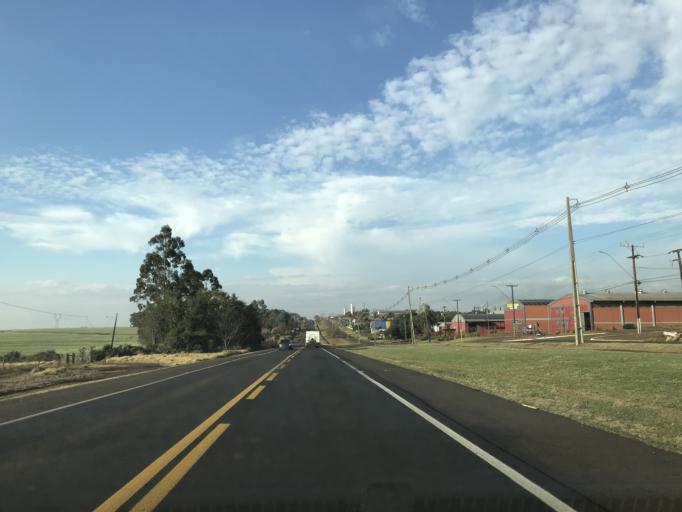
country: BR
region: Parana
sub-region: Cascavel
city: Cascavel
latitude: -25.0428
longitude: -53.6045
